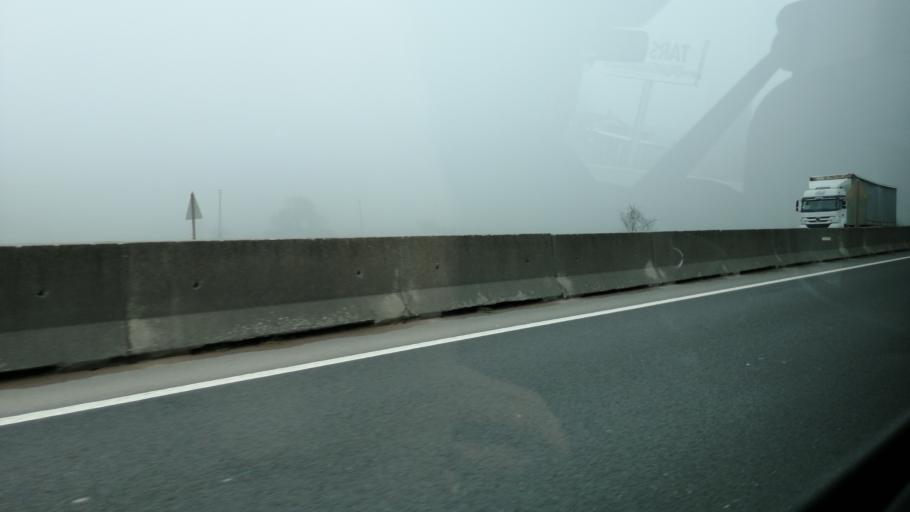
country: TR
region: Yalova
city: Taskopru
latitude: 40.6792
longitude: 29.3724
